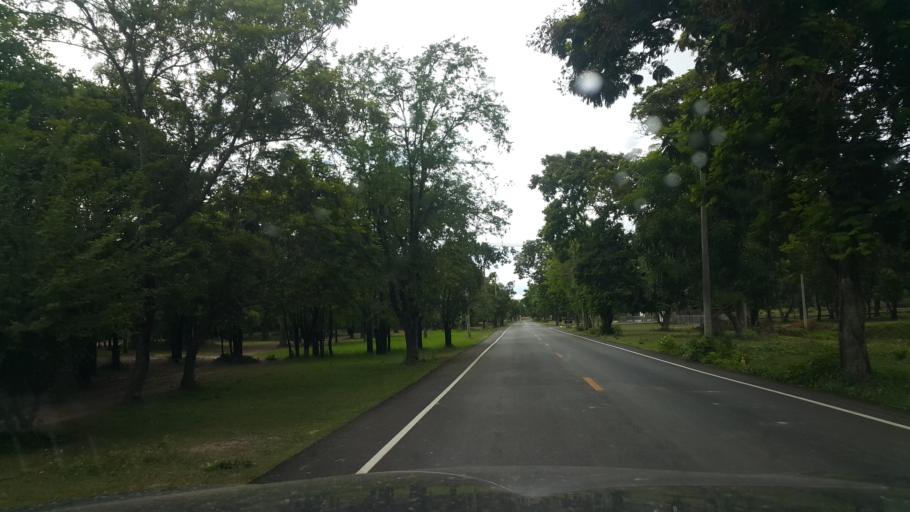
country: TH
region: Sukhothai
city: Ban Na
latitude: 17.0283
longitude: 99.6961
